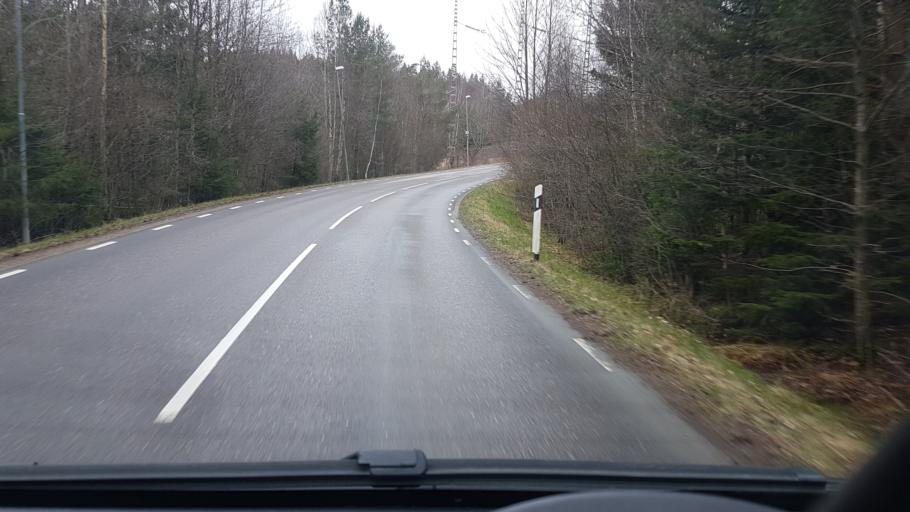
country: SE
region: Vaestra Goetaland
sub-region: Lerums Kommun
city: Stenkullen
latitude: 57.8077
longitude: 12.3347
